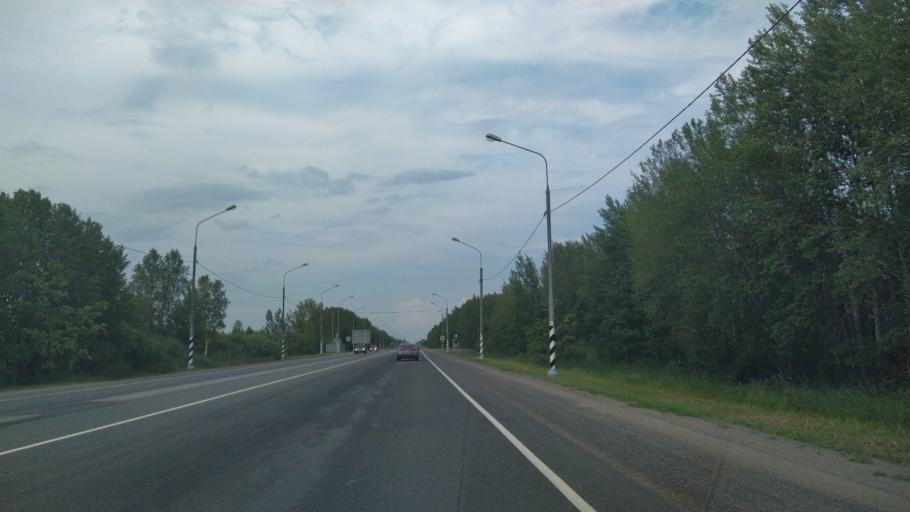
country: RU
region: Novgorod
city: Pankovka
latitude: 58.4430
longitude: 31.1203
